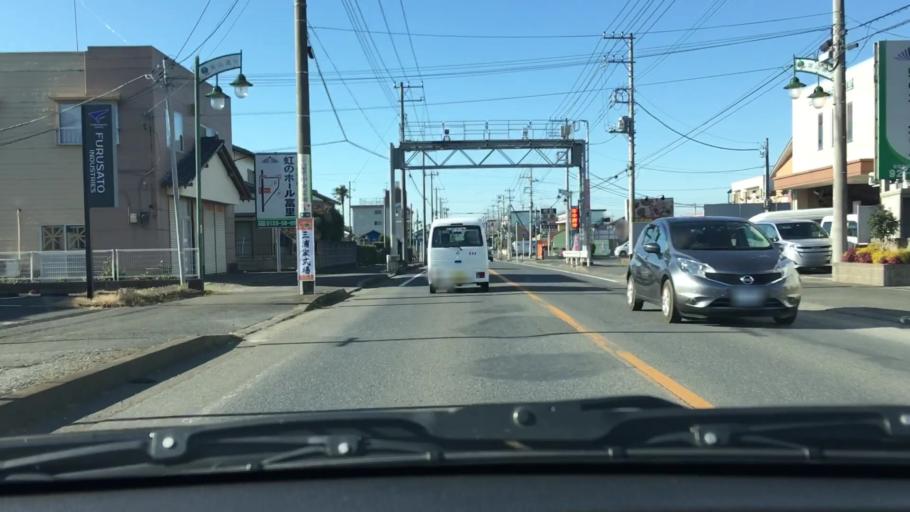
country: JP
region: Chiba
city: Narita
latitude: 35.7255
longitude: 140.3604
